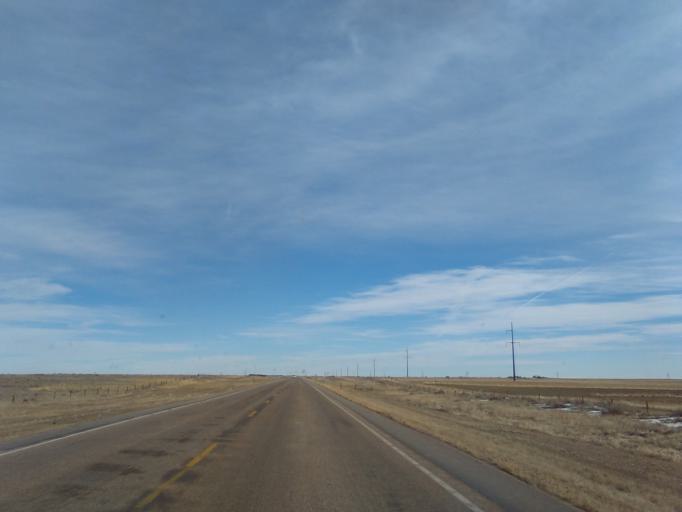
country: US
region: Wyoming
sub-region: Laramie County
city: Pine Bluffs
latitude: 41.4253
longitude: -104.3907
